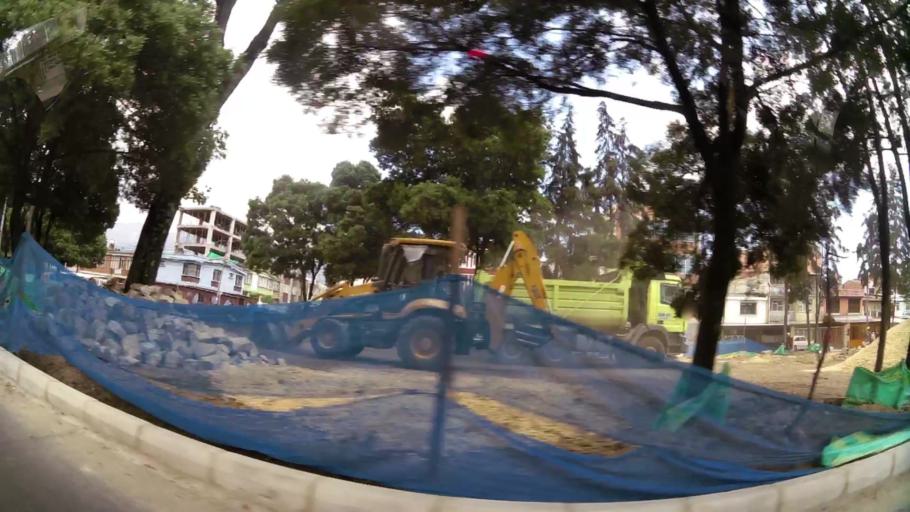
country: CO
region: Bogota D.C.
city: Bogota
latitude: 4.5814
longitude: -74.0983
